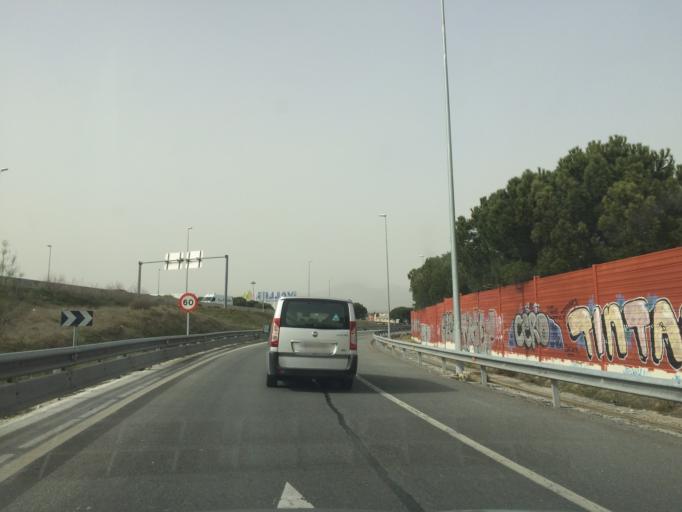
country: ES
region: Madrid
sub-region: Provincia de Madrid
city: Collado-Villalba
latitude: 40.6354
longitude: -4.0057
